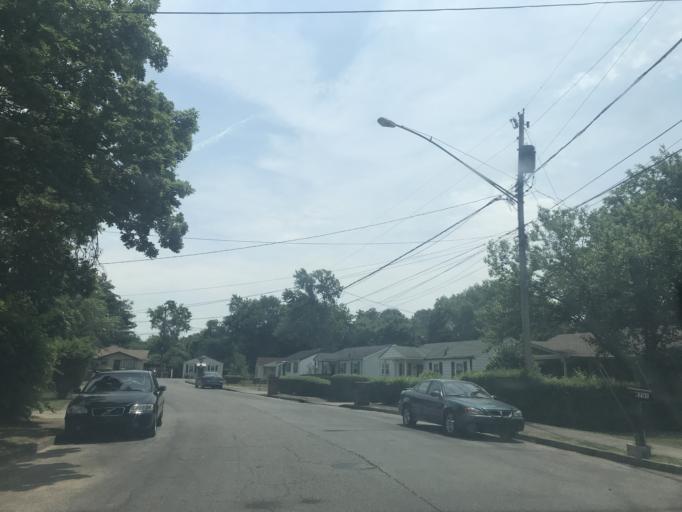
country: US
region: Tennessee
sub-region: Davidson County
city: Nashville
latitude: 36.1846
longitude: -86.8211
